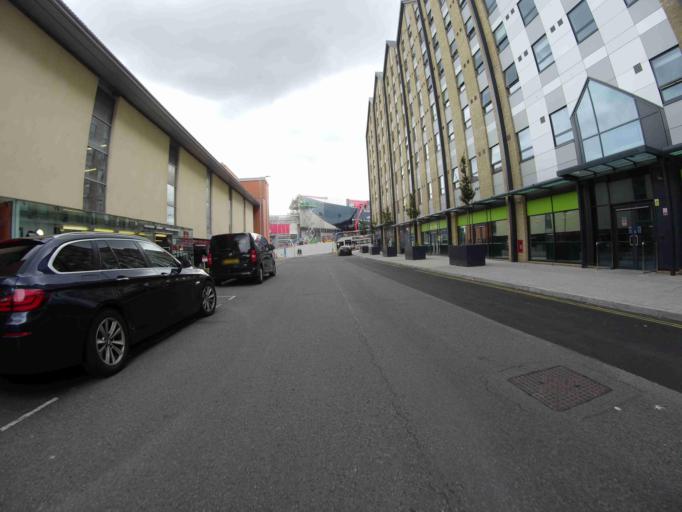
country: GB
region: England
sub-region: Devon
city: Exeter
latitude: 50.7264
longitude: -3.5224
